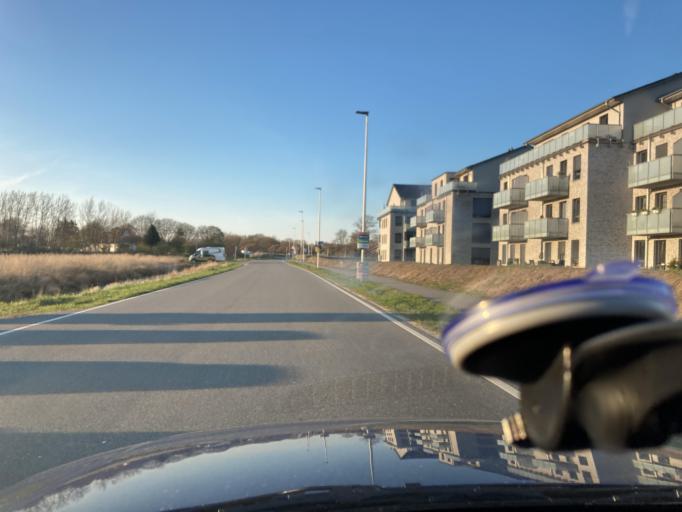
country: DE
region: Schleswig-Holstein
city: Lohe-Rickelshof
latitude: 54.1962
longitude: 9.0732
